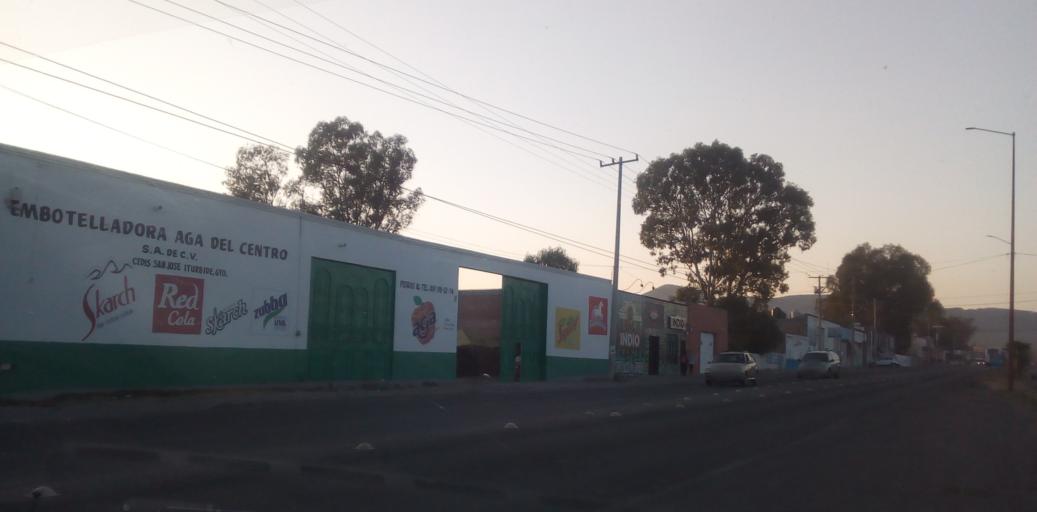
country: MX
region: Guanajuato
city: San Jose Iturbide
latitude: 21.0105
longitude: -100.3881
